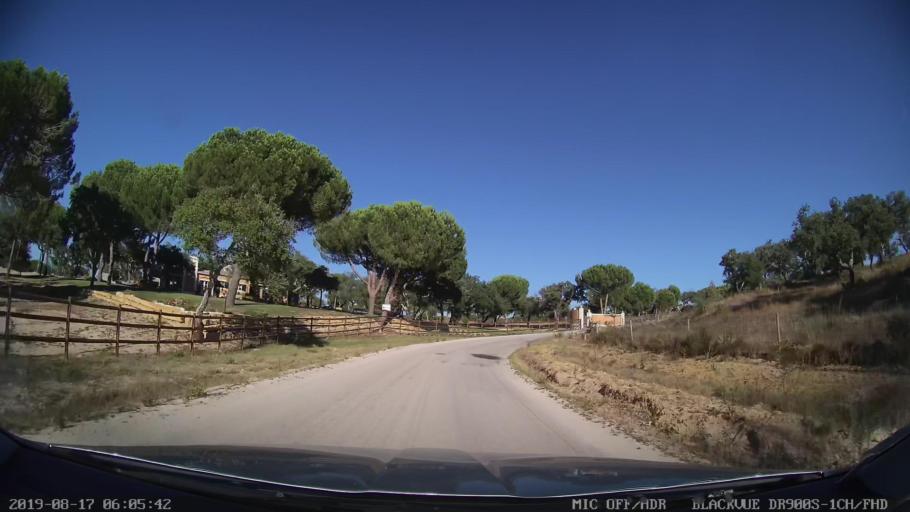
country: PT
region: Santarem
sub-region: Benavente
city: Poceirao
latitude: 38.8478
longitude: -8.6951
